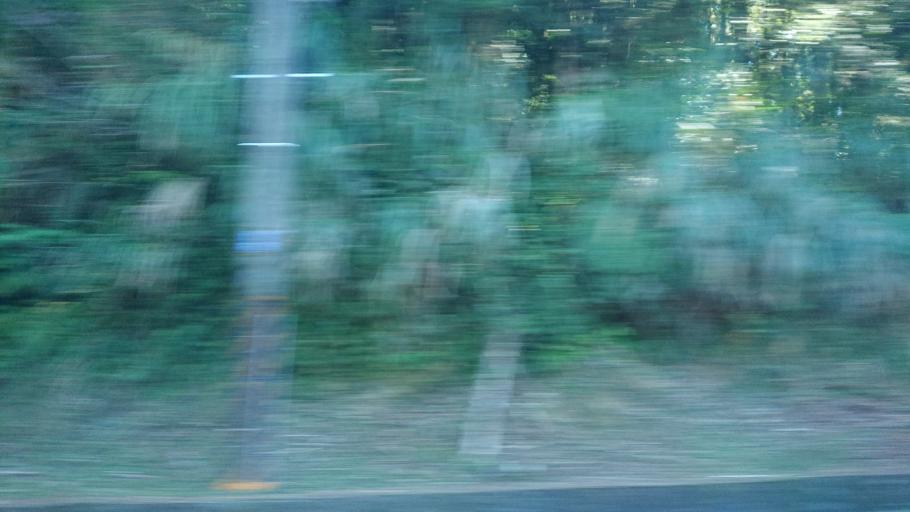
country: TW
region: Taiwan
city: Lugu
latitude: 23.4982
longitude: 120.7807
